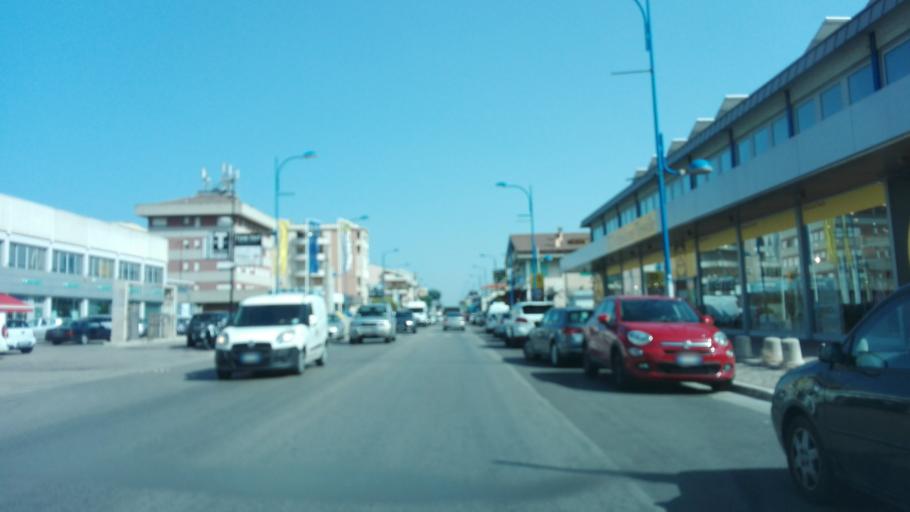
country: IT
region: Abruzzo
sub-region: Provincia di Pescara
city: Montesilvano Marina
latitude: 42.5030
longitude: 14.1663
